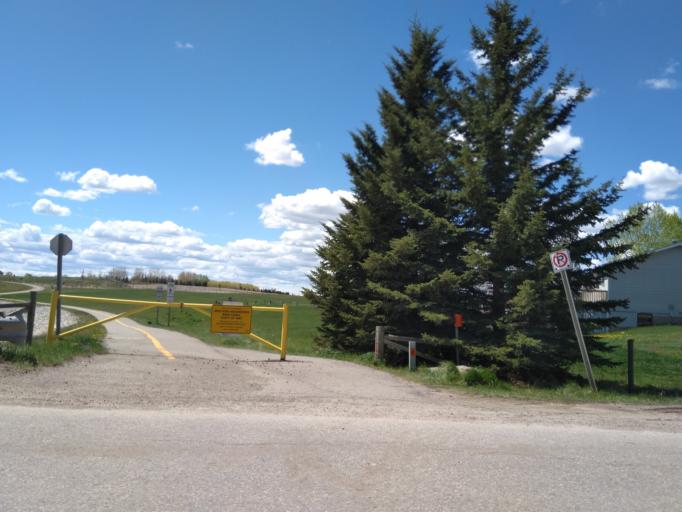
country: CA
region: Alberta
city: Chestermere
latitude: 51.0185
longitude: -113.8410
